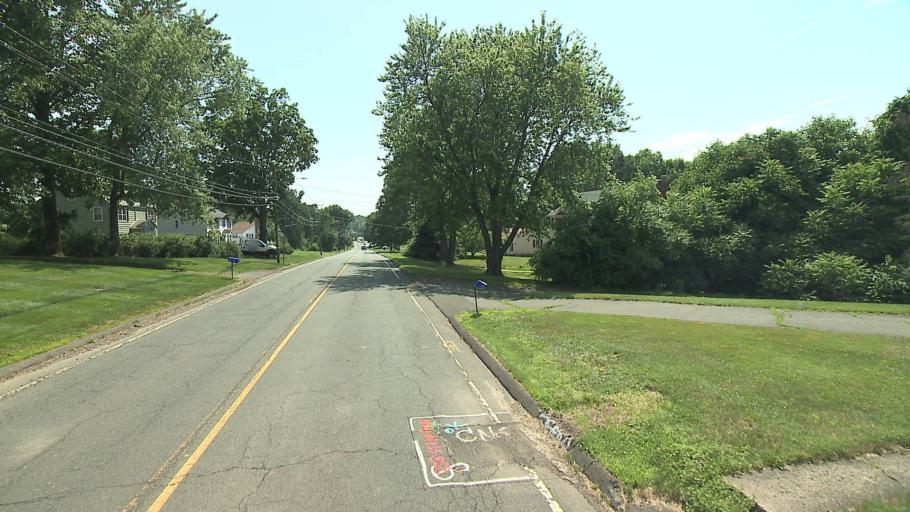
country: US
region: Connecticut
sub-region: Hartford County
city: Kensington
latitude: 41.6294
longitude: -72.7404
